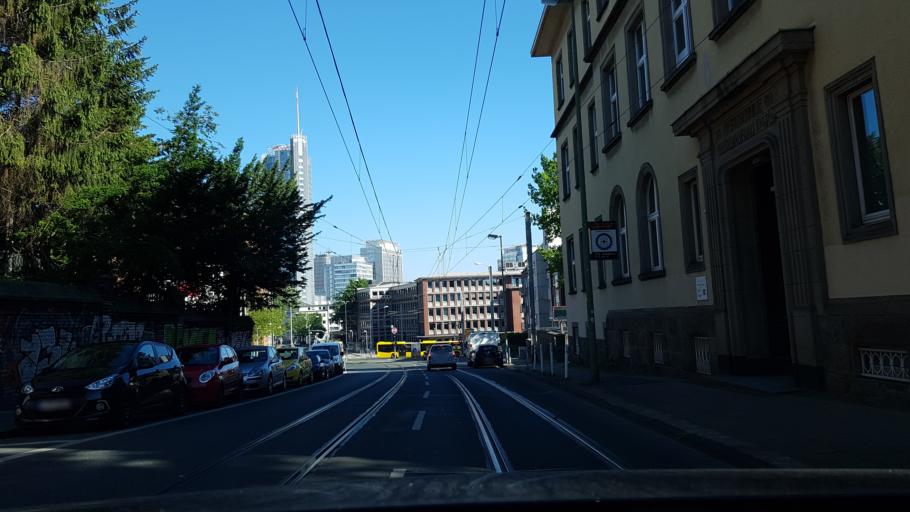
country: DE
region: North Rhine-Westphalia
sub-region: Regierungsbezirk Dusseldorf
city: Essen
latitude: 51.4442
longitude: 7.0185
